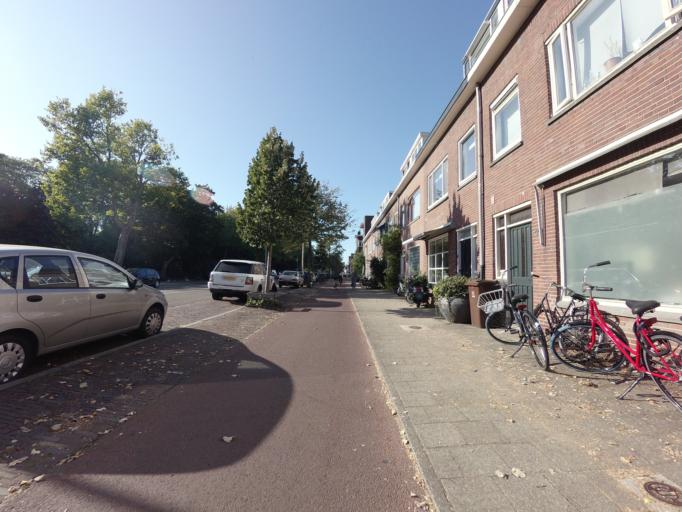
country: NL
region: Utrecht
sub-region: Gemeente Utrecht
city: Utrecht
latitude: 52.1073
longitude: 5.0890
